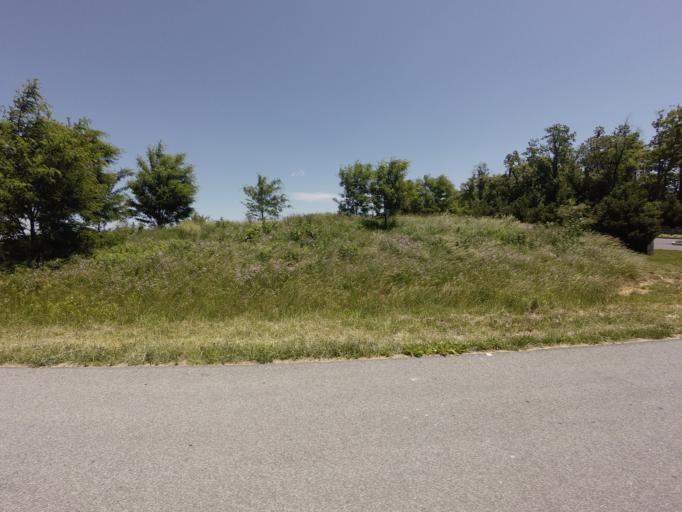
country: US
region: West Virginia
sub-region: Jefferson County
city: Ranson
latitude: 39.3187
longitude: -77.8238
